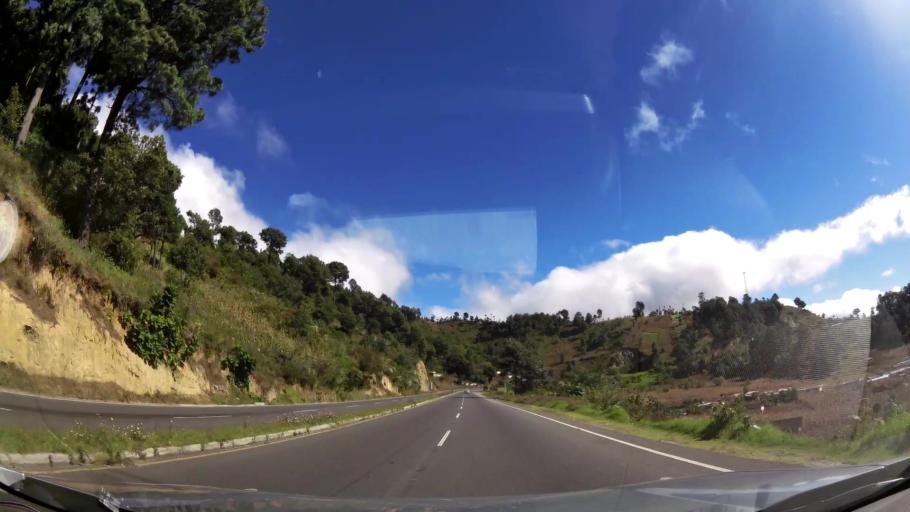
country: GT
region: Solola
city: Solola
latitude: 14.8282
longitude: -91.1923
